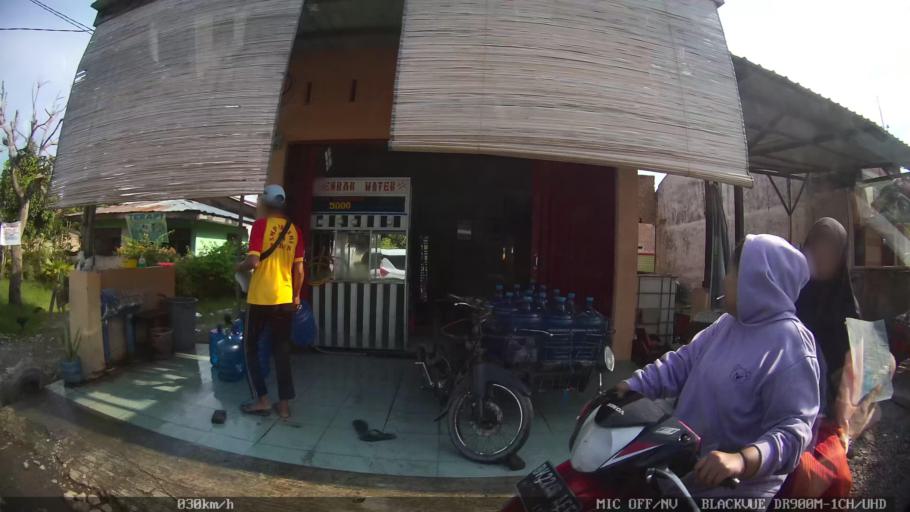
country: ID
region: North Sumatra
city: Percut
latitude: 3.5938
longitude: 98.7781
